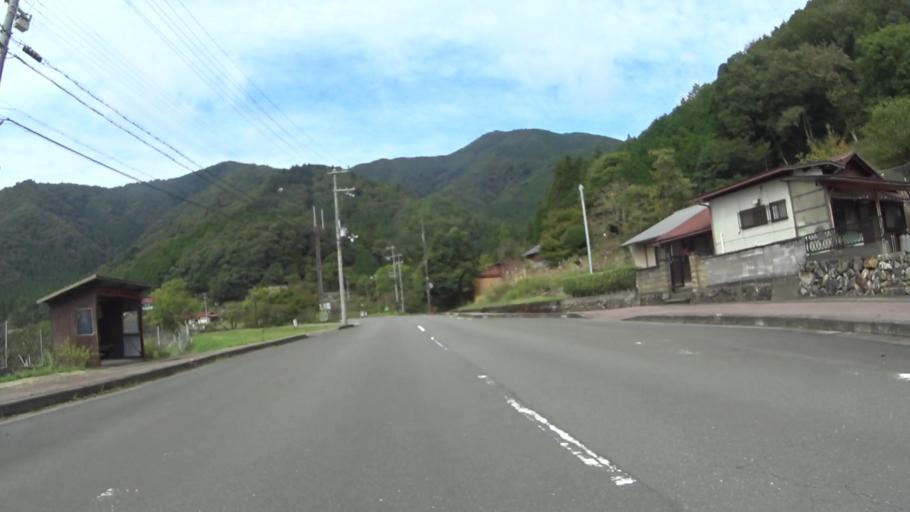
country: JP
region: Kyoto
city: Ayabe
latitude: 35.2698
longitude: 135.4720
